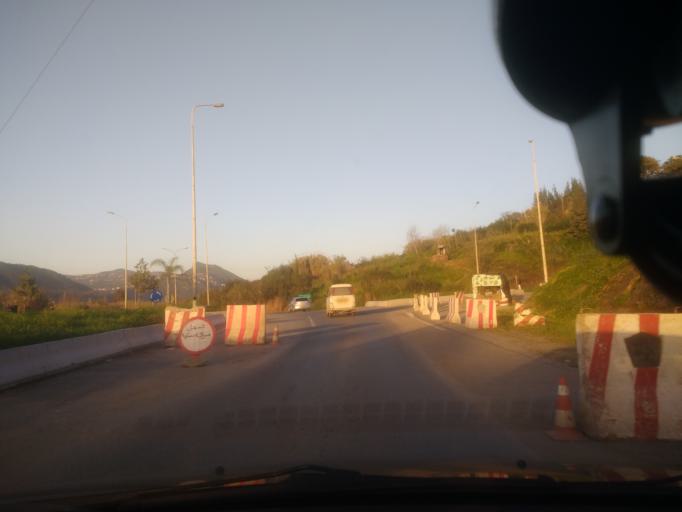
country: DZ
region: Tizi Ouzou
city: Tizi Ouzou
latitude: 36.7472
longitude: 4.0137
